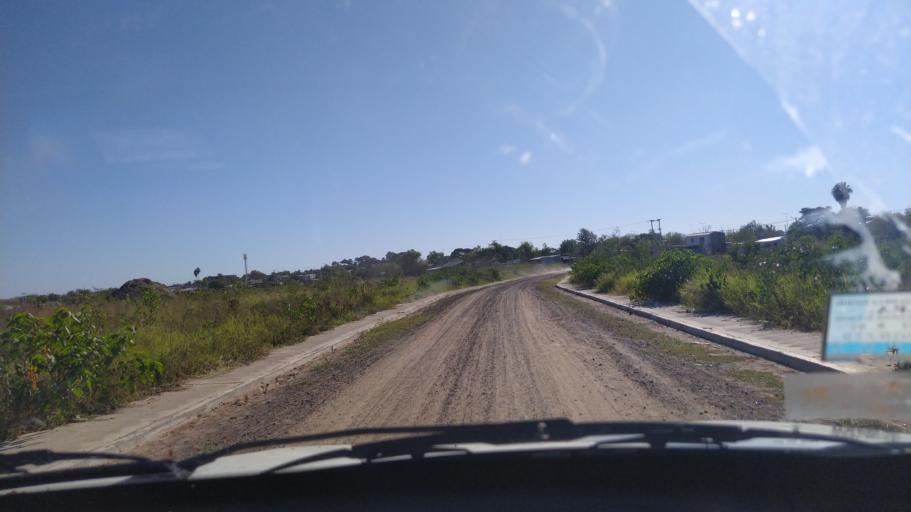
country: AR
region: Corrientes
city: Corrientes
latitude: -27.5003
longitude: -58.8014
